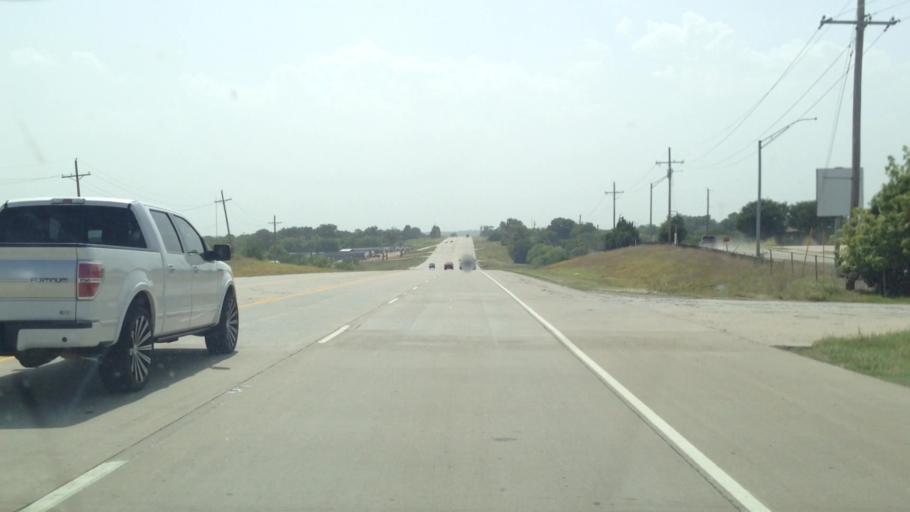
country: US
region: Texas
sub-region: Collin County
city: Farmersville
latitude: 33.1591
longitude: -96.3945
